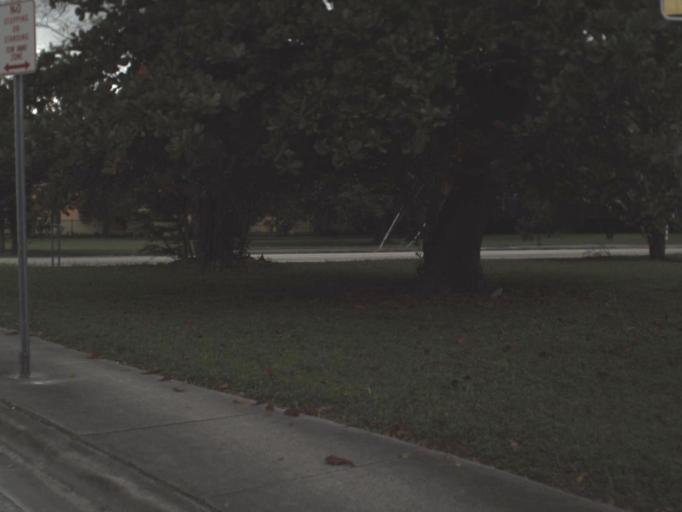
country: US
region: Florida
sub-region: Miami-Dade County
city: Miami
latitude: 25.7801
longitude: -80.2003
